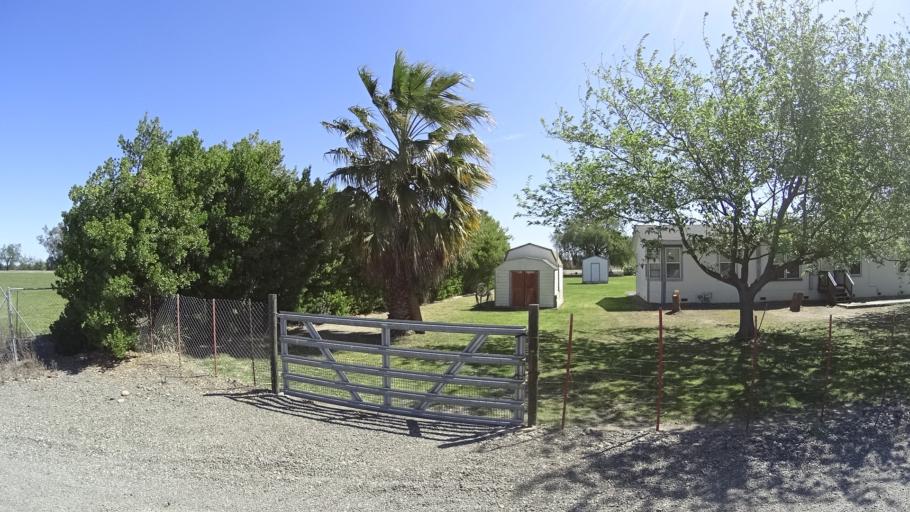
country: US
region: California
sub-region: Glenn County
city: Orland
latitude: 39.7489
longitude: -122.1381
